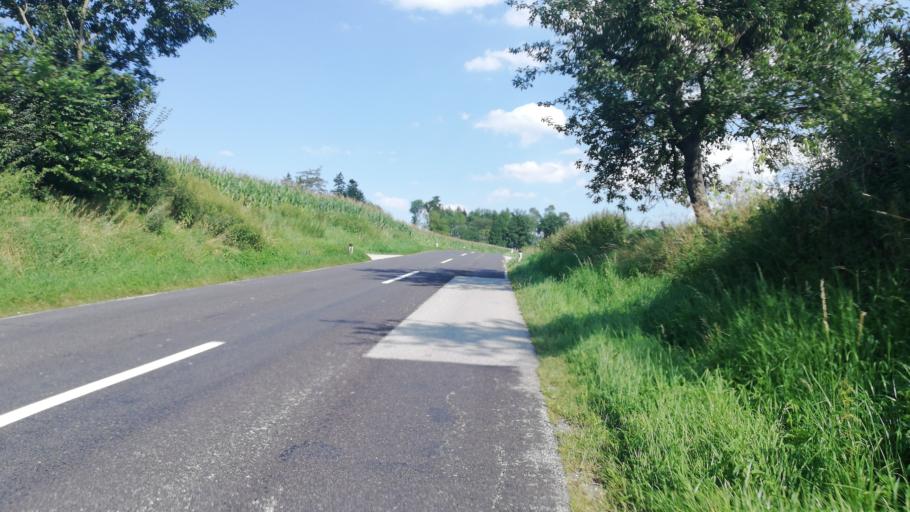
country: AT
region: Upper Austria
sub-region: Wels-Land
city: Gunskirchen
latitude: 48.1581
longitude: 13.9245
